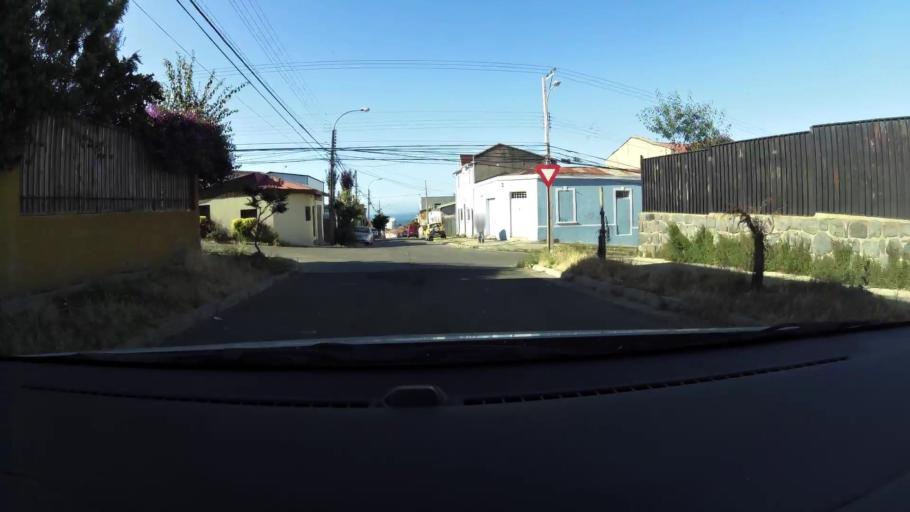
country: CL
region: Valparaiso
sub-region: Provincia de Valparaiso
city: Vina del Mar
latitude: -33.0301
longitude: -71.5674
